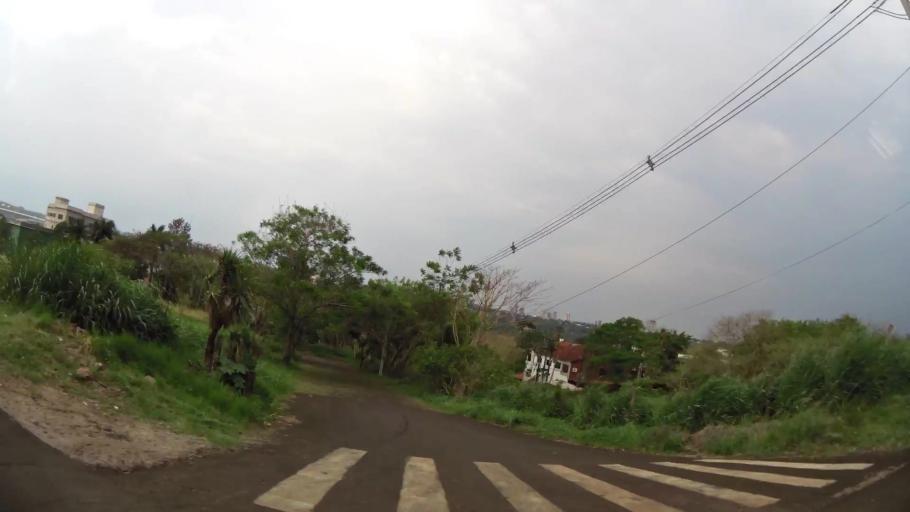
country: PY
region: Alto Parana
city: Ciudad del Este
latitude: -25.5172
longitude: -54.6064
